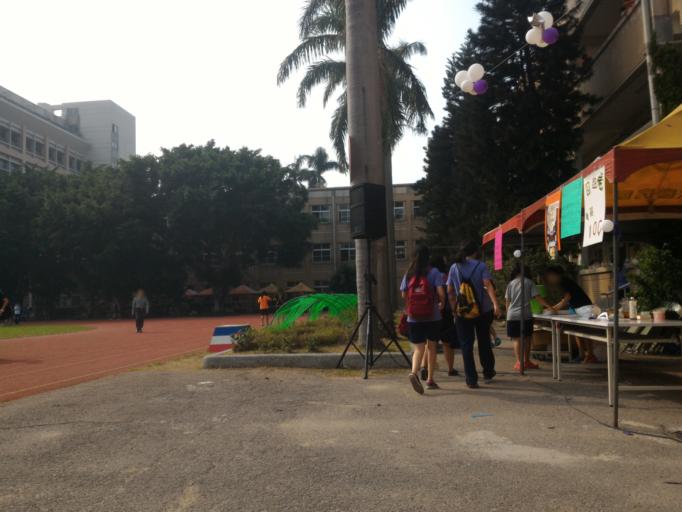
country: TW
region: Taipei
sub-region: Taipei
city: Banqiao
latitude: 25.0284
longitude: 121.4971
